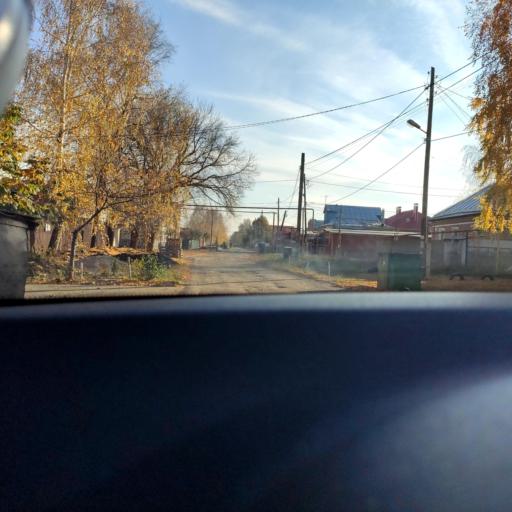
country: RU
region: Samara
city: Petra-Dubrava
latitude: 53.2565
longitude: 50.3245
